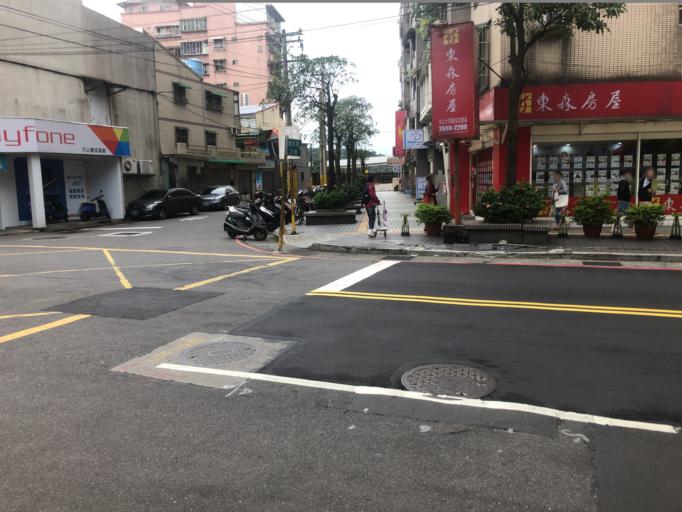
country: TW
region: Taiwan
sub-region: Keelung
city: Keelung
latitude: 25.0729
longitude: 121.6645
